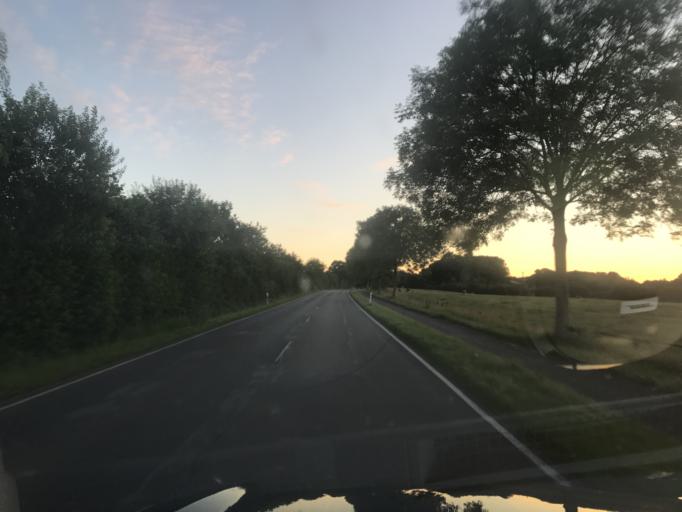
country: DE
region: Schleswig-Holstein
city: Agethorst
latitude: 54.0246
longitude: 9.4283
